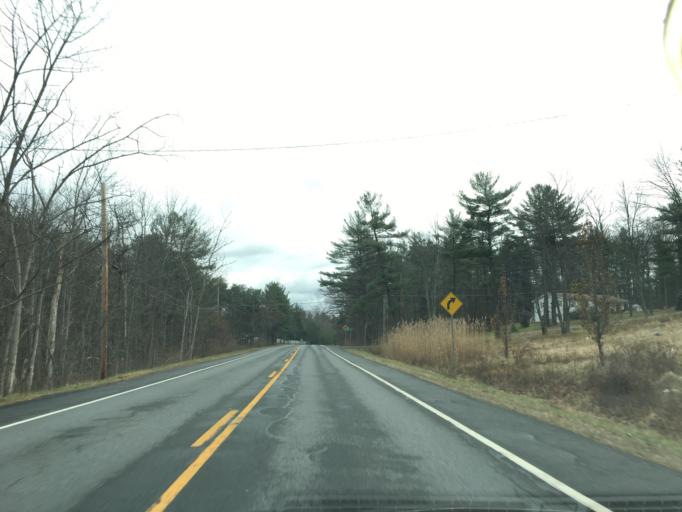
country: US
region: New York
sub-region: Rensselaer County
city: Averill Park
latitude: 42.6490
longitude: -73.5536
